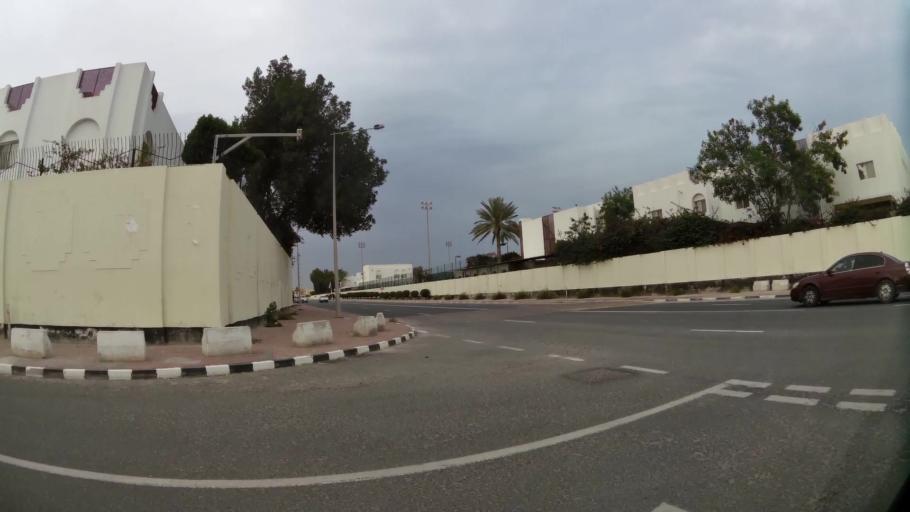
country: QA
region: Baladiyat ad Dawhah
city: Doha
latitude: 25.3262
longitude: 51.5128
